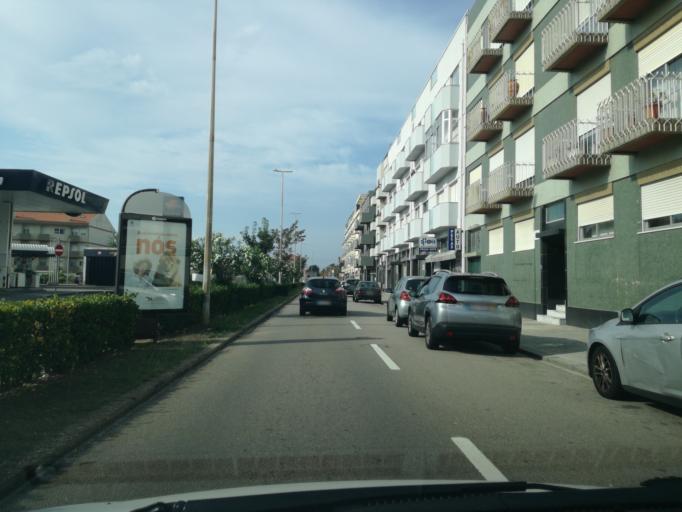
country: PT
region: Aveiro
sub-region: Espinho
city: Espinho
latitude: 41.0104
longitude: -8.6379
